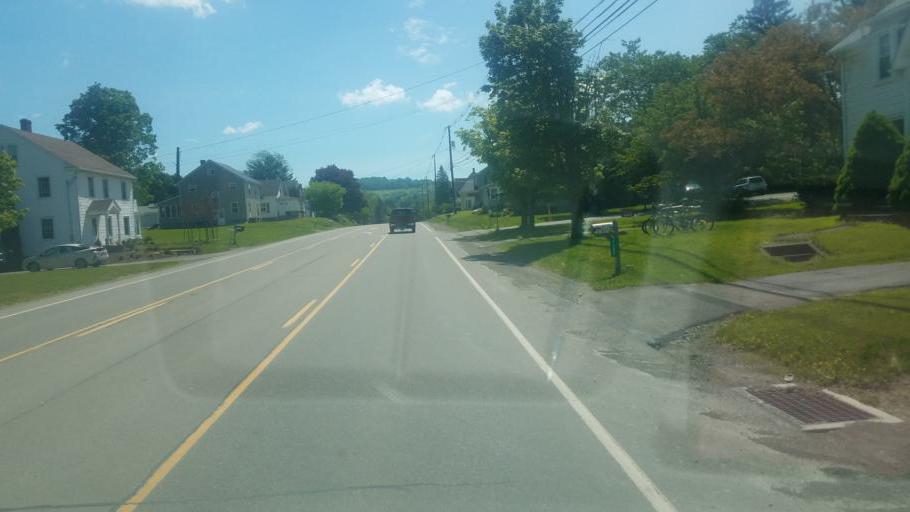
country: US
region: Pennsylvania
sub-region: Tioga County
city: Wellsboro
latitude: 41.7456
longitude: -77.2792
